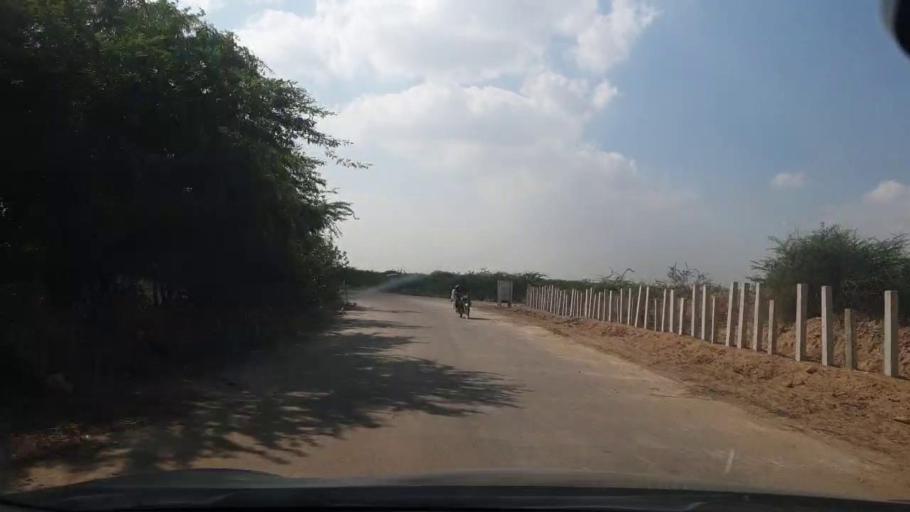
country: PK
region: Sindh
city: Malir Cantonment
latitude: 25.0217
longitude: 67.3553
